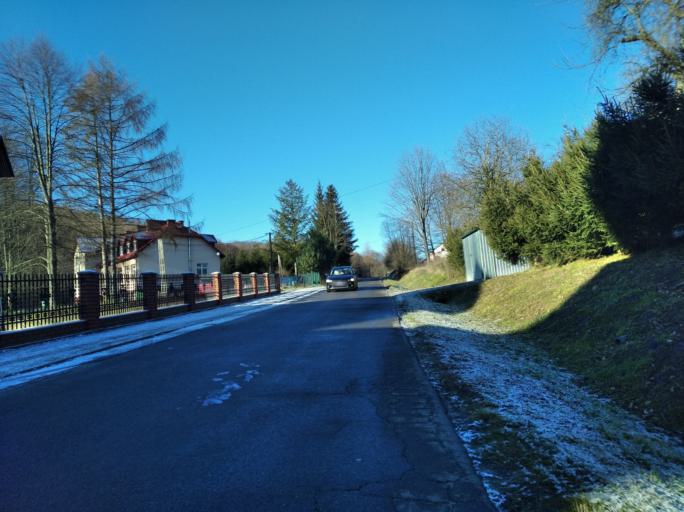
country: PL
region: Subcarpathian Voivodeship
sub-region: Powiat strzyzowski
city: Czudec
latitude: 49.9550
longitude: 21.7669
